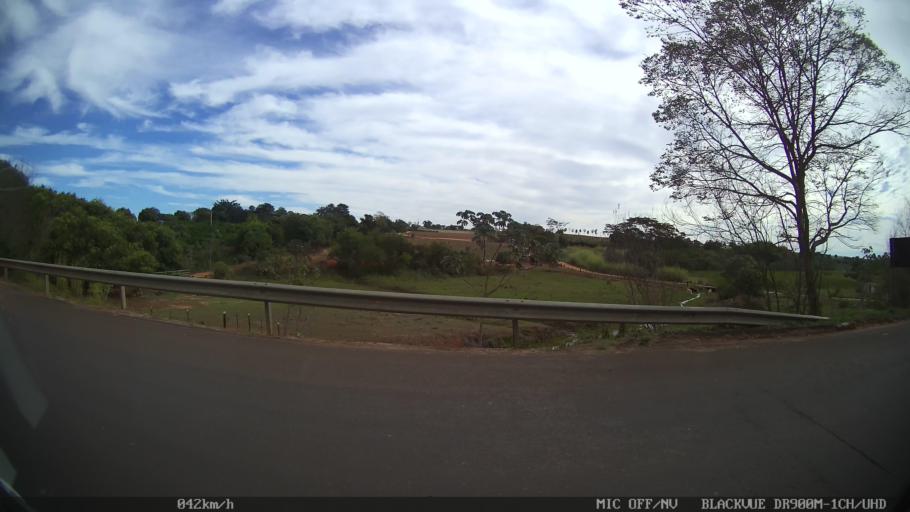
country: BR
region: Sao Paulo
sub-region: Santa Adelia
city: Santa Adelia
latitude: -21.3704
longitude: -48.7486
